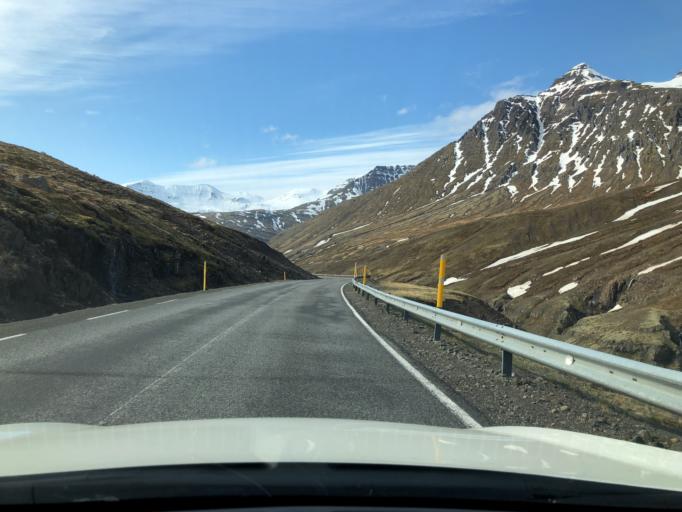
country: IS
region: East
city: Reydarfjoerdur
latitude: 65.0502
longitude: -14.3497
